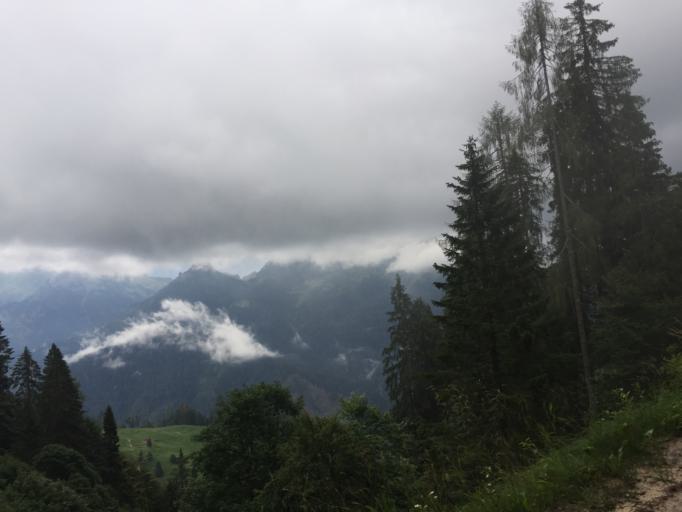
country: IT
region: Friuli Venezia Giulia
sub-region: Provincia di Udine
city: Forni Avoltri
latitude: 46.5670
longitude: 12.7759
